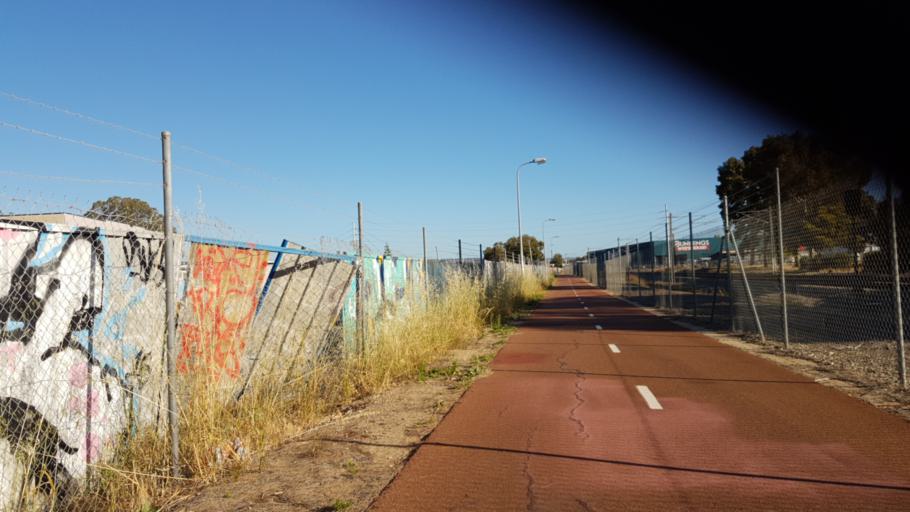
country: AU
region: Western Australia
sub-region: Gosnells
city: Maddington
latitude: -32.0435
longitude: 115.9757
